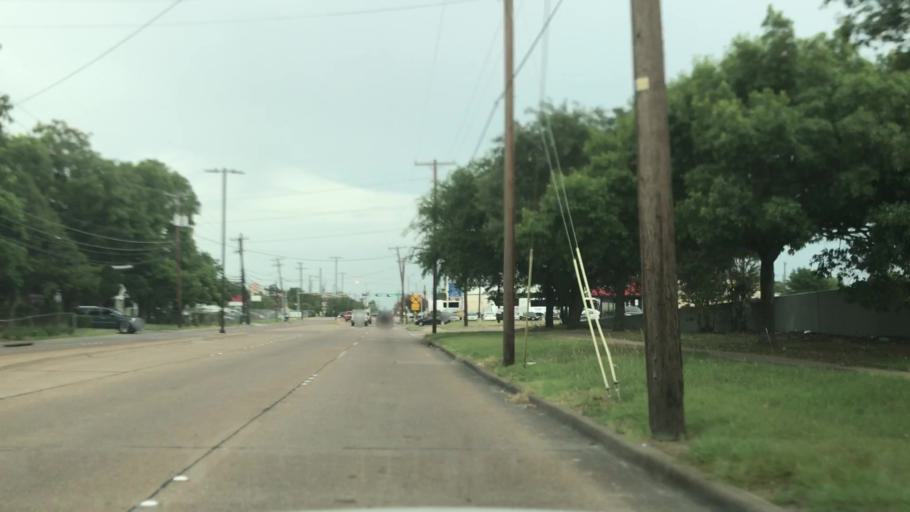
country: US
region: Texas
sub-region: Dallas County
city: Garland
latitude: 32.8788
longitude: -96.6624
